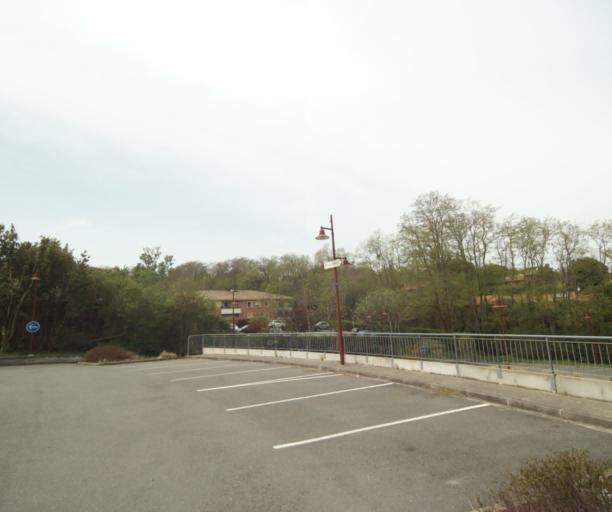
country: FR
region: Midi-Pyrenees
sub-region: Departement de la Haute-Garonne
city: Pechabou
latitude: 43.5006
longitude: 1.5077
